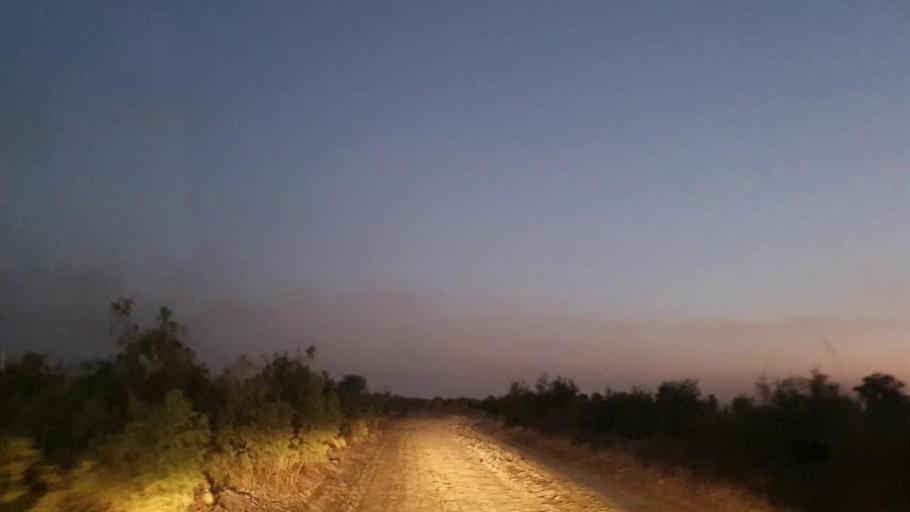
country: PK
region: Sindh
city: Nawabshah
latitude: 26.3302
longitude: 68.3753
